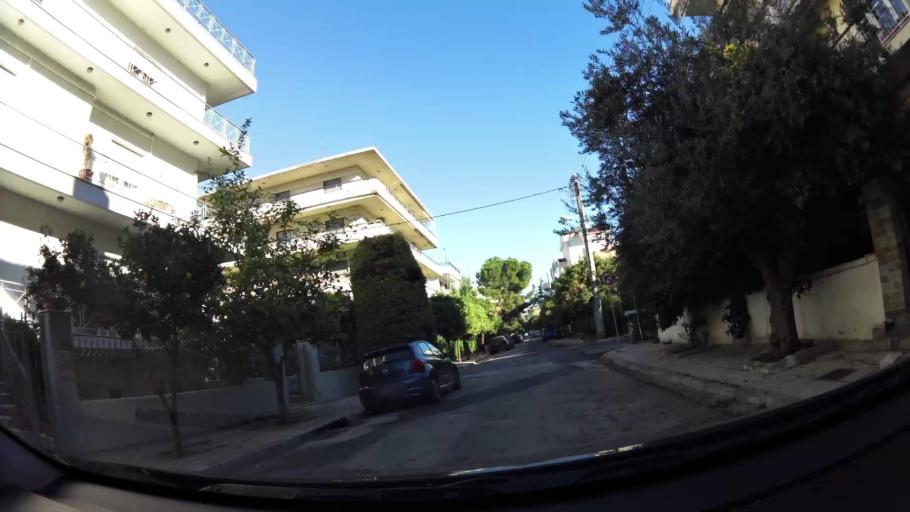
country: GR
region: Attica
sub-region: Nomarchia Athinas
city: Khalandrion
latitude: 38.0154
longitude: 23.8057
